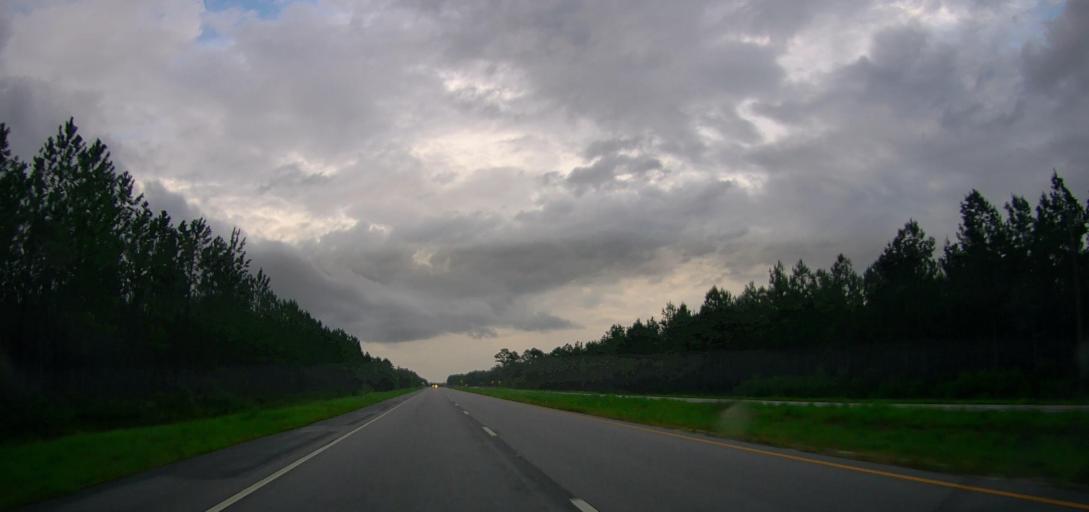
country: US
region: Georgia
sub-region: Ware County
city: Deenwood
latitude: 31.1287
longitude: -82.5174
